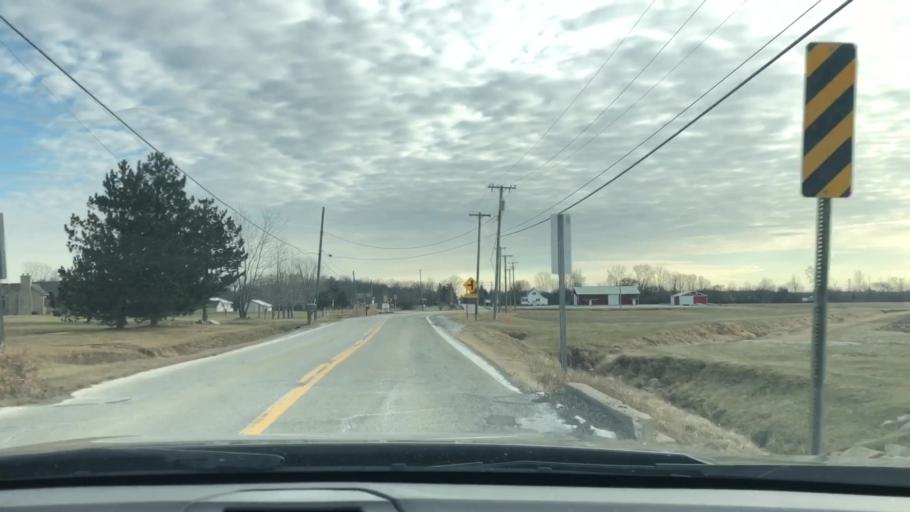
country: US
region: Michigan
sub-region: Macomb County
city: Romeo
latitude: 42.7307
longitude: -82.9797
